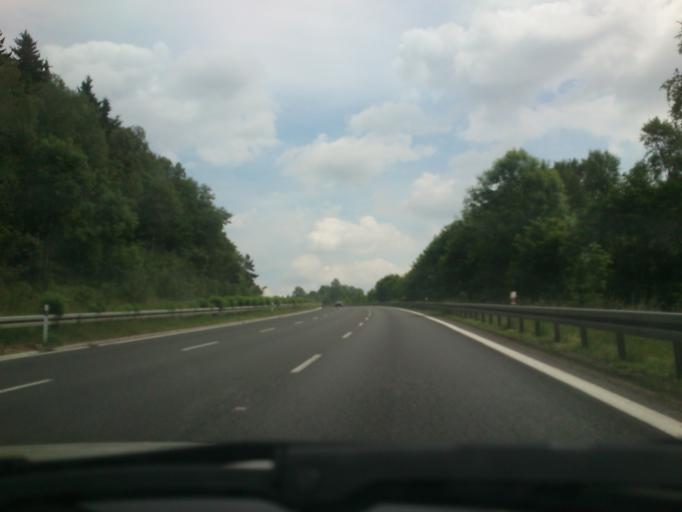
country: CZ
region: Liberecky
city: Hodkovice nad Mohelkou
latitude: 50.7129
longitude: 15.0785
